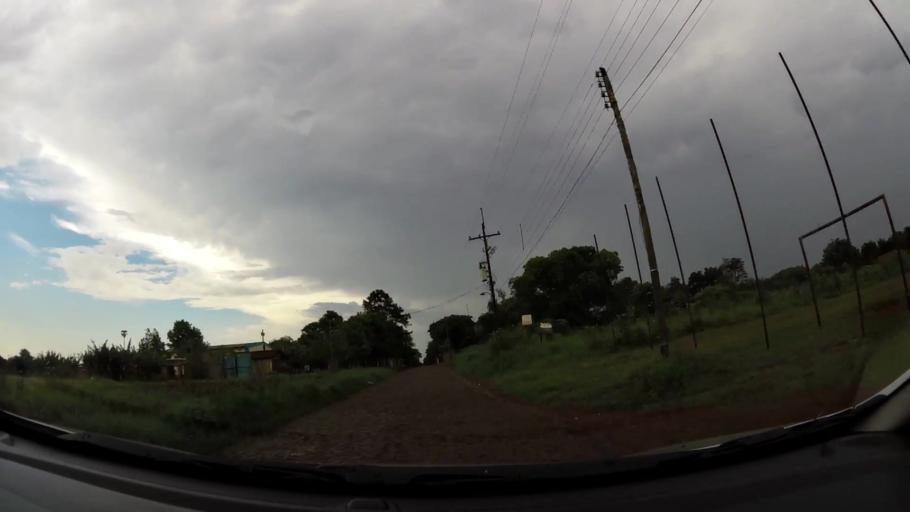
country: PY
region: Alto Parana
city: Presidente Franco
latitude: -25.5531
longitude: -54.6505
